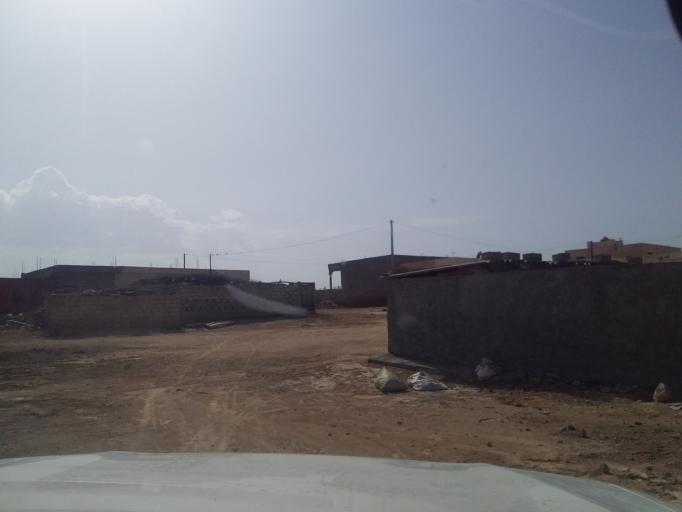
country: TN
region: Qabis
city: Gabes
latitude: 33.6330
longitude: 10.2867
